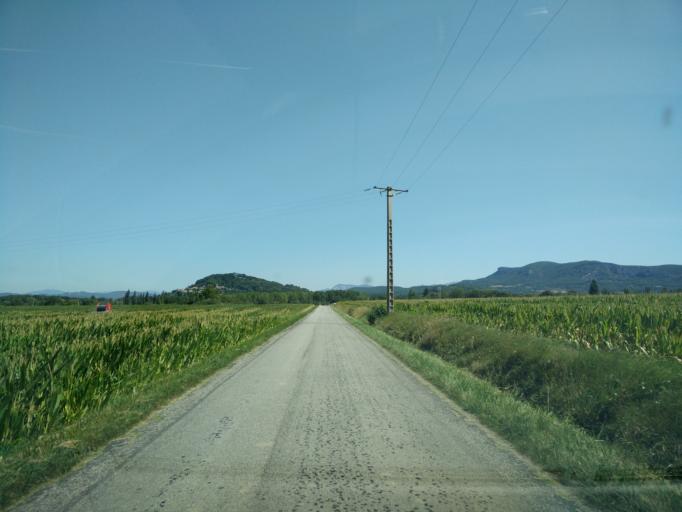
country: FR
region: Rhone-Alpes
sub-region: Departement de la Drome
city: La Begude-de-Mazenc
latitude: 44.5343
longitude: 4.9217
